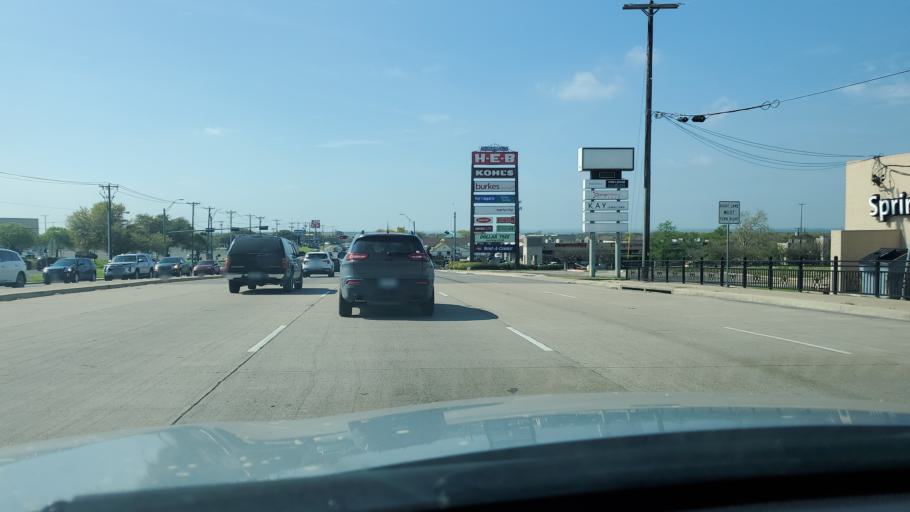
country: US
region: Texas
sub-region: Bell County
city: Temple
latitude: 31.0719
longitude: -97.3686
